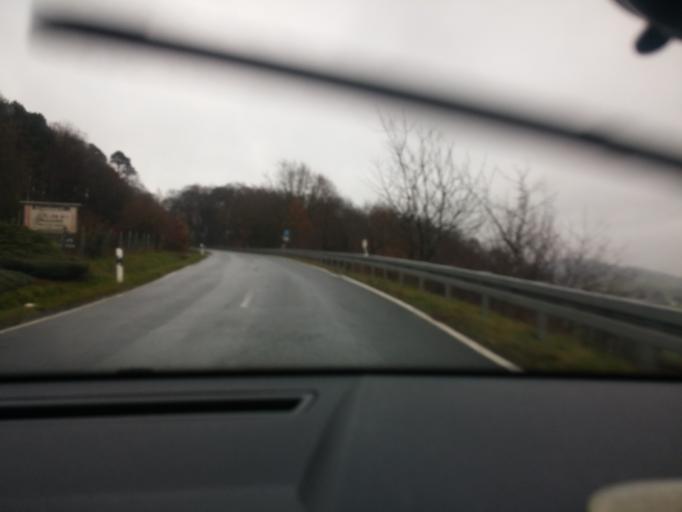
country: DE
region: Hesse
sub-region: Regierungsbezirk Darmstadt
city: Brensbach
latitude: 49.7659
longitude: 8.8836
